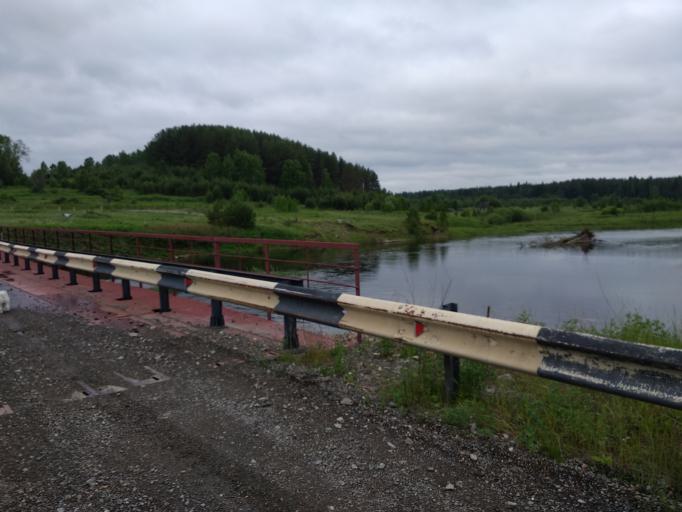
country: RU
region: Sverdlovsk
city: Karpinsk
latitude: 59.3909
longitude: 59.9480
